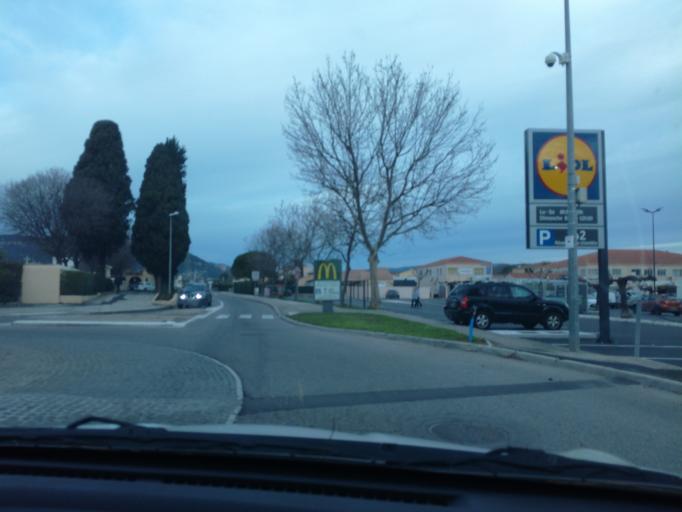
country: FR
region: Provence-Alpes-Cote d'Azur
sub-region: Departement du Var
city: La Crau
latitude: 43.1524
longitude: 6.0725
